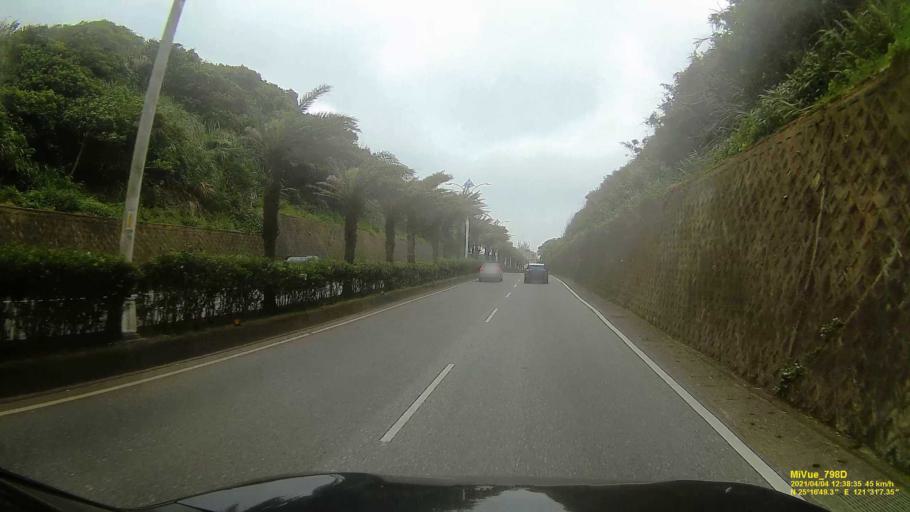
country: TW
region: Taipei
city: Taipei
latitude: 25.2801
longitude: 121.5186
